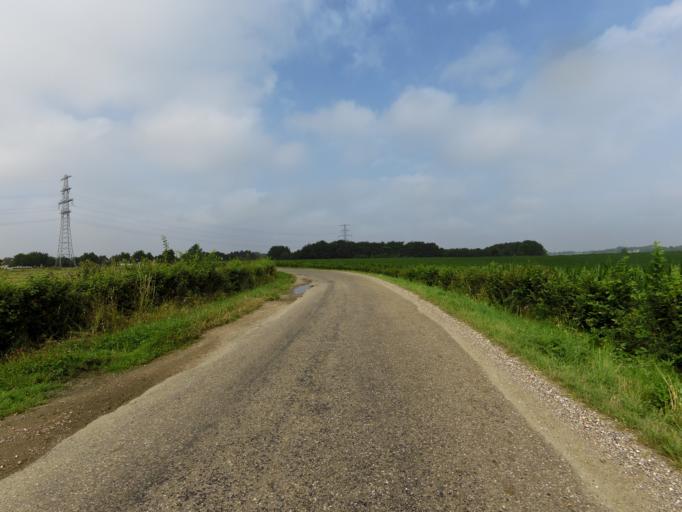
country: NL
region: Limburg
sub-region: Gemeente Voerendaal
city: Klimmen
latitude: 50.8690
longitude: 5.8734
